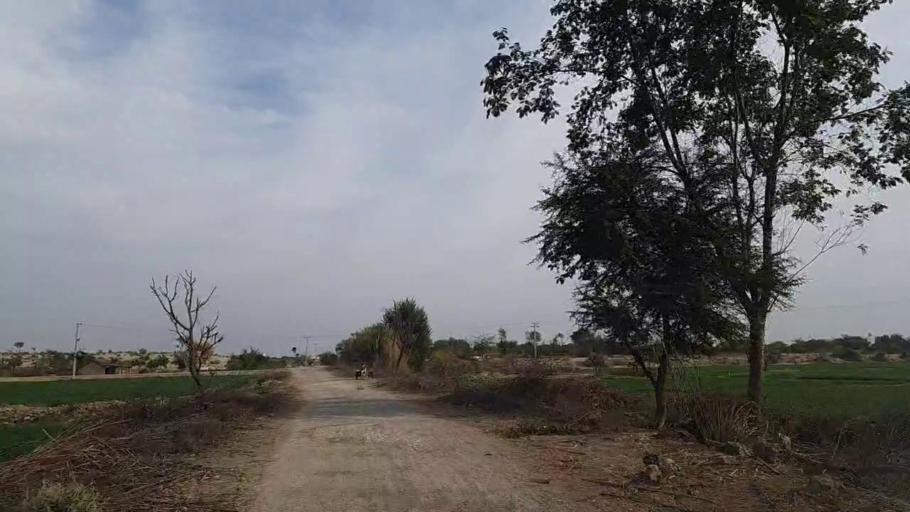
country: PK
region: Sindh
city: Jam Sahib
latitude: 26.4354
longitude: 68.6344
